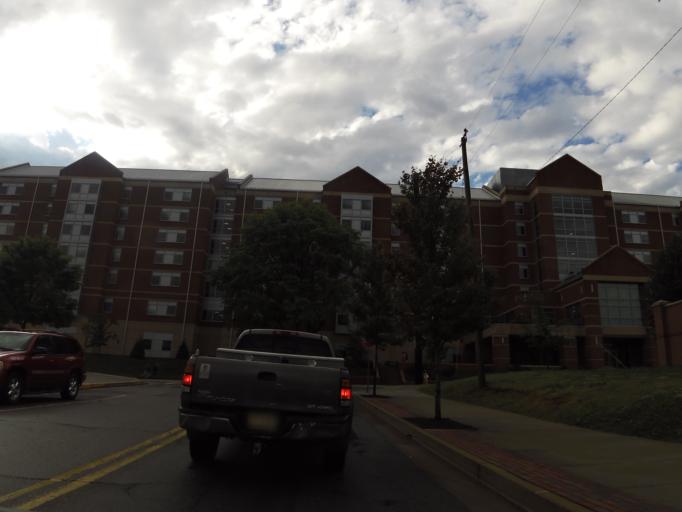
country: US
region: Tennessee
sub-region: Knox County
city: Knoxville
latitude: 35.9522
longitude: -83.9321
